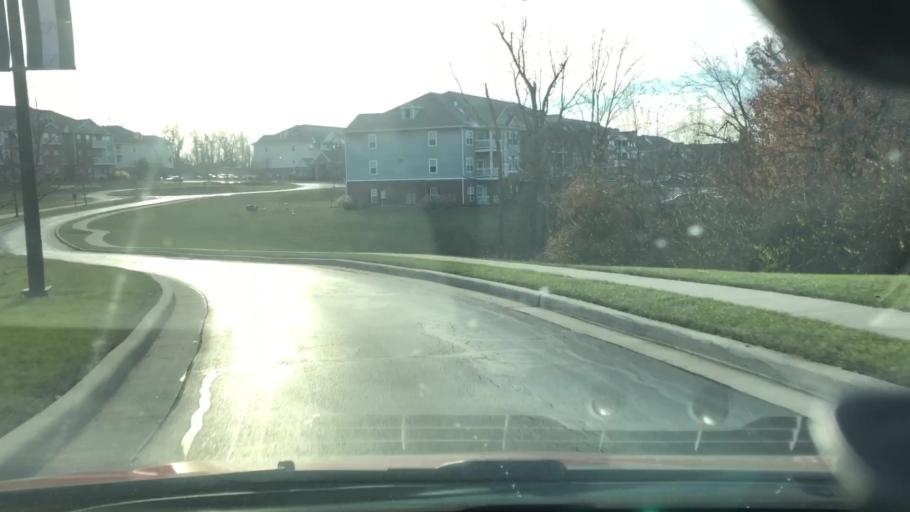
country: US
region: Ohio
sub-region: Montgomery County
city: Riverside
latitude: 39.7704
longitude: -84.0802
